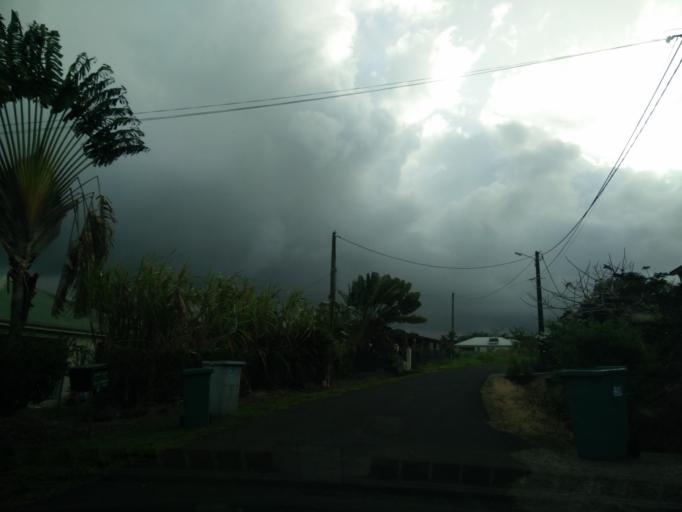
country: GP
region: Guadeloupe
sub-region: Guadeloupe
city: Petit-Bourg
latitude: 16.1800
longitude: -61.6096
